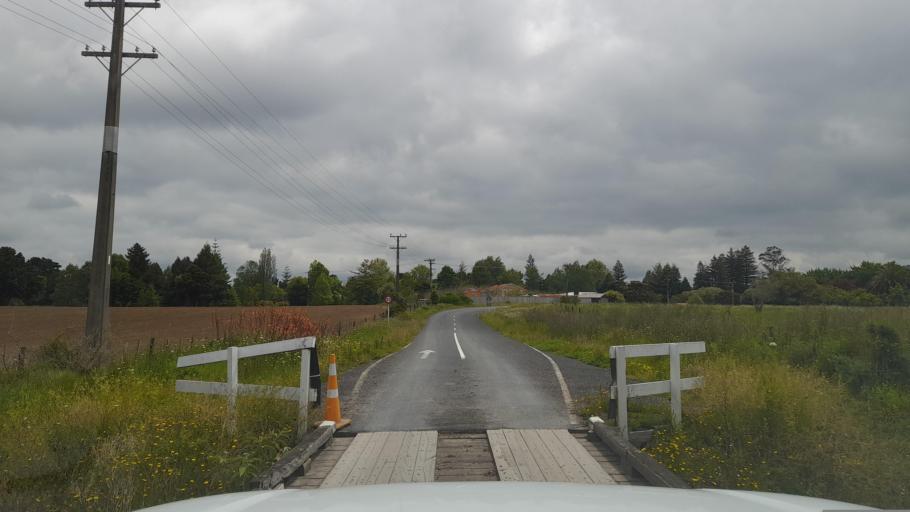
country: NZ
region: Northland
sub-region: Far North District
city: Waimate North
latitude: -35.4035
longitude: 173.8104
